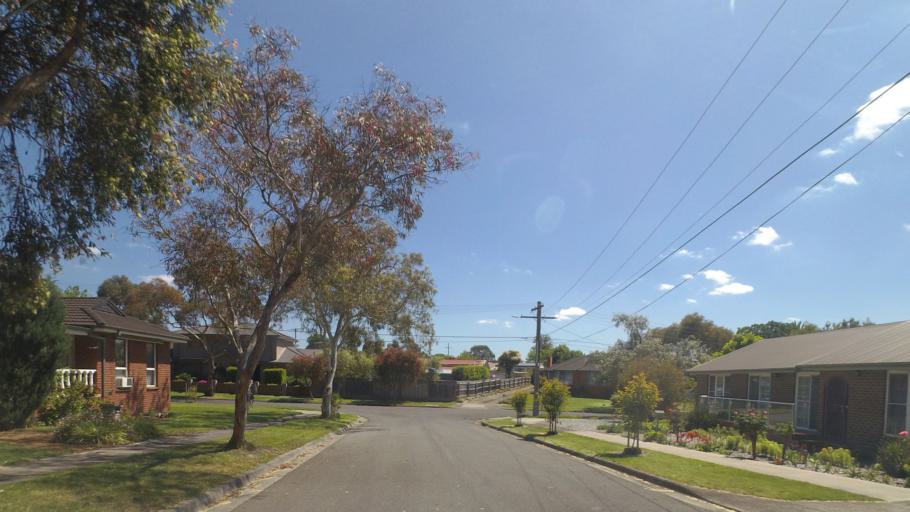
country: AU
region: Victoria
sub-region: Knox
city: Bayswater
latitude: -37.8542
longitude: 145.2705
